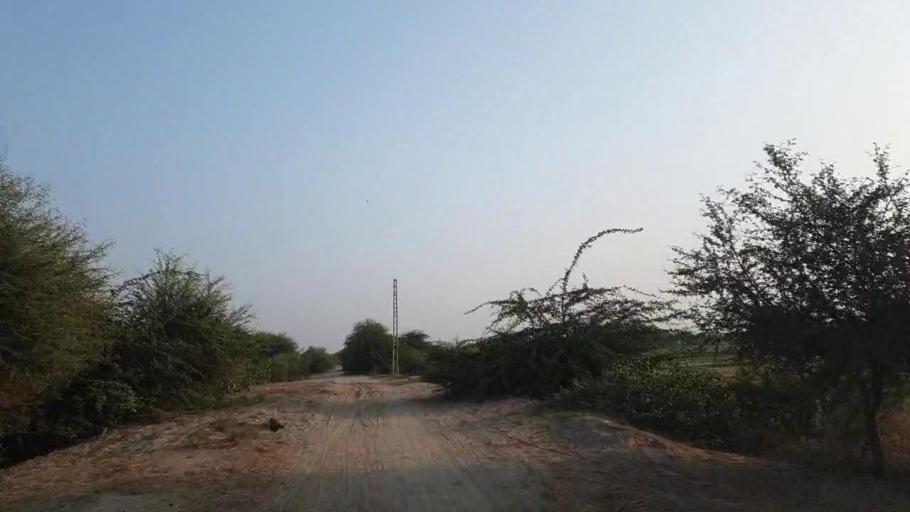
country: PK
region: Sindh
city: Kario
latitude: 24.8621
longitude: 68.6241
